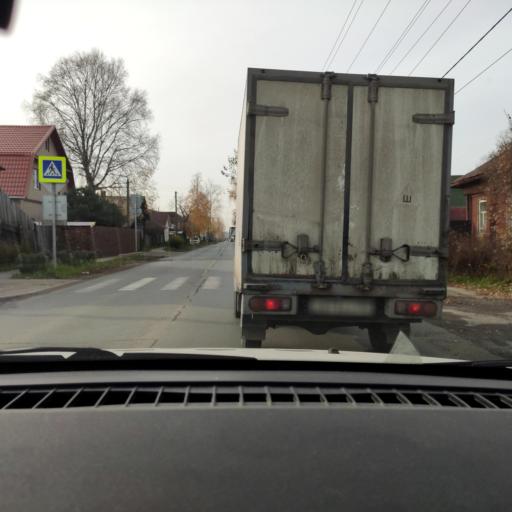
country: RU
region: Perm
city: Perm
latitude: 58.0486
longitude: 56.3327
